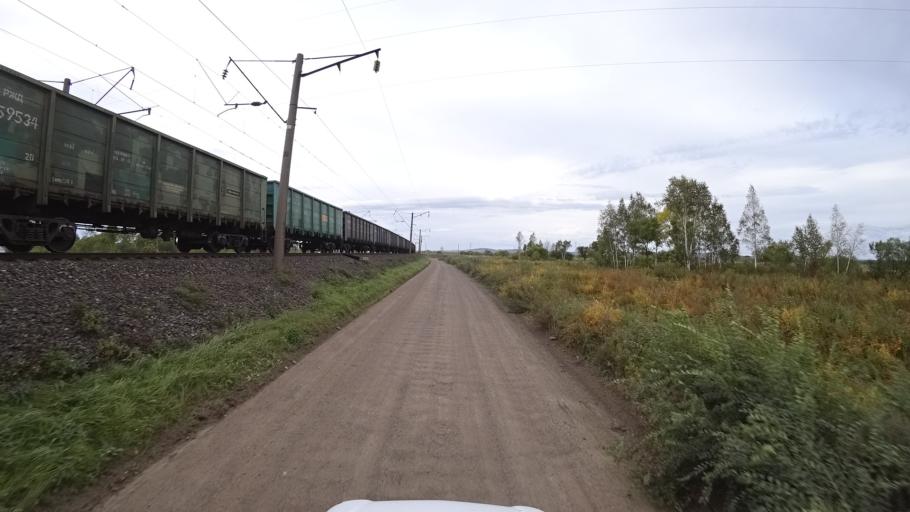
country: RU
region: Amur
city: Arkhara
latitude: 49.3688
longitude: 130.1422
